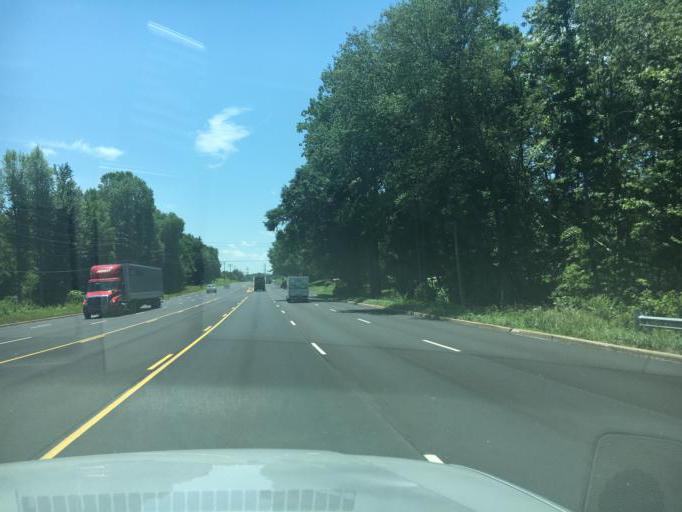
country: US
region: South Carolina
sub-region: Greenville County
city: Berea
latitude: 34.9227
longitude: -82.4578
